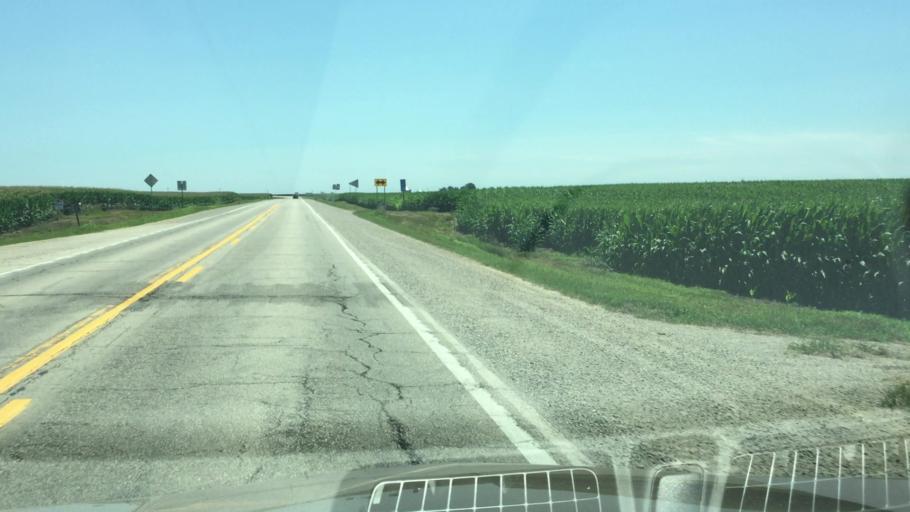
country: US
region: Iowa
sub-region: Cedar County
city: Mechanicsville
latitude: 41.8937
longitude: -91.2207
